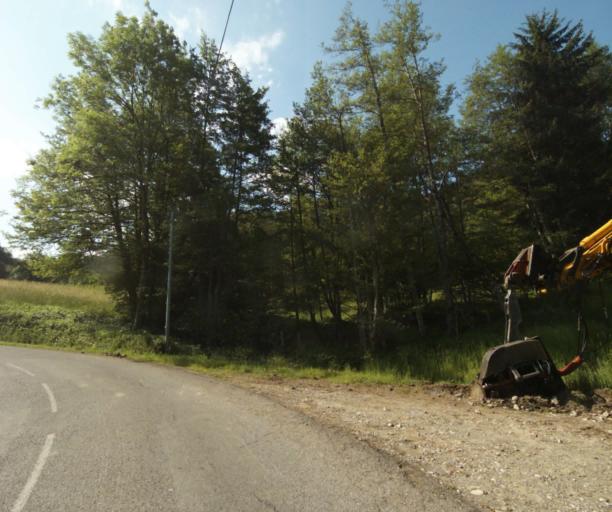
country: FR
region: Rhone-Alpes
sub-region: Departement de la Haute-Savoie
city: Lyaud
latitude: 46.3029
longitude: 6.4976
